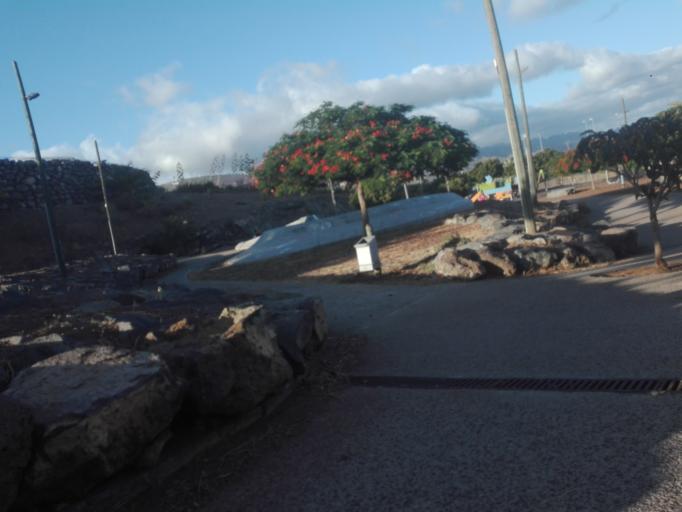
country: ES
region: Canary Islands
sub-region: Provincia de Santa Cruz de Tenerife
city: Santa Cruz de Tenerife
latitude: 28.4561
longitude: -16.2774
